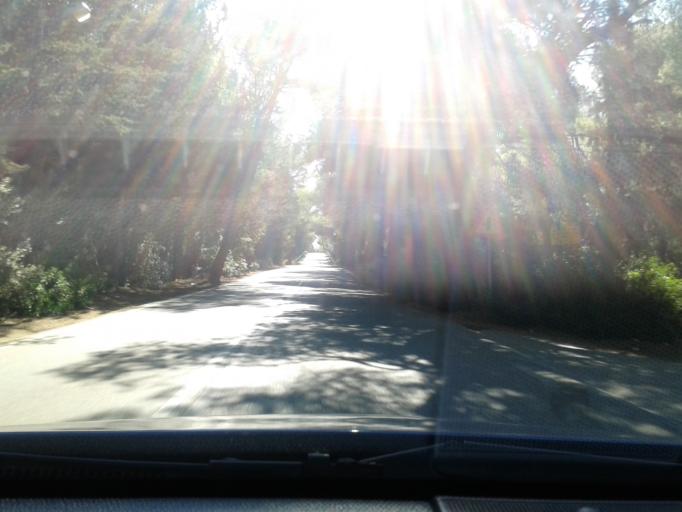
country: GR
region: Attica
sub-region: Nomarchia Anatolikis Attikis
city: Varybobi
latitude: 38.1140
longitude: 23.8016
